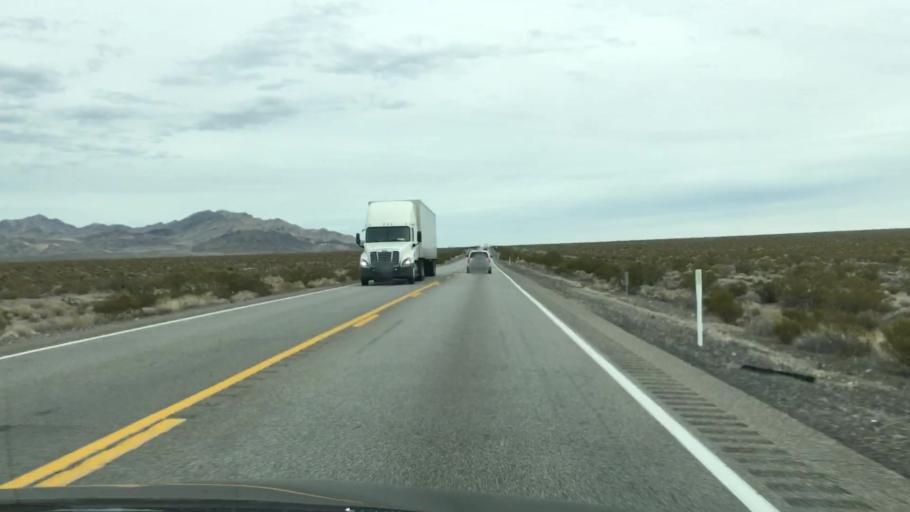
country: US
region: Nevada
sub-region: Nye County
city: Pahrump
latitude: 36.5912
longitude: -116.0356
